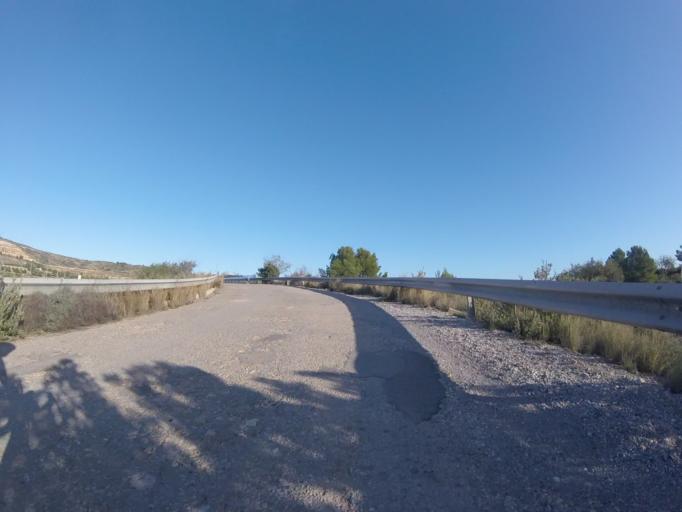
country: ES
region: Valencia
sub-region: Provincia de Castello
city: Torreblanca
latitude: 40.2255
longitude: 0.1984
